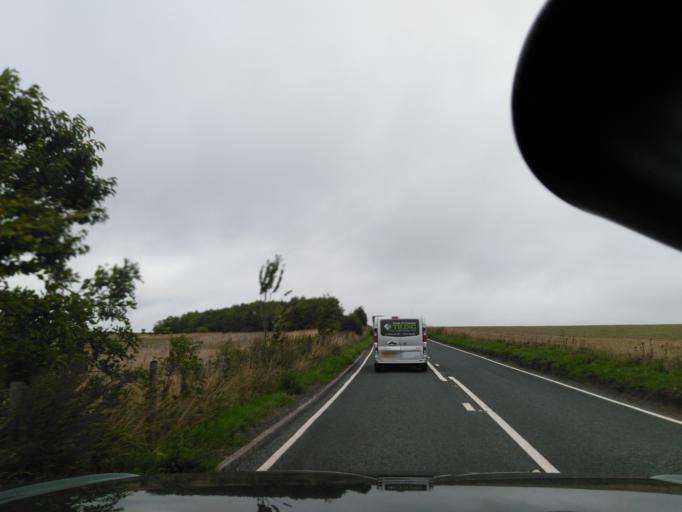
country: GB
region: England
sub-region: Wiltshire
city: Chicklade
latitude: 51.1339
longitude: -2.1618
